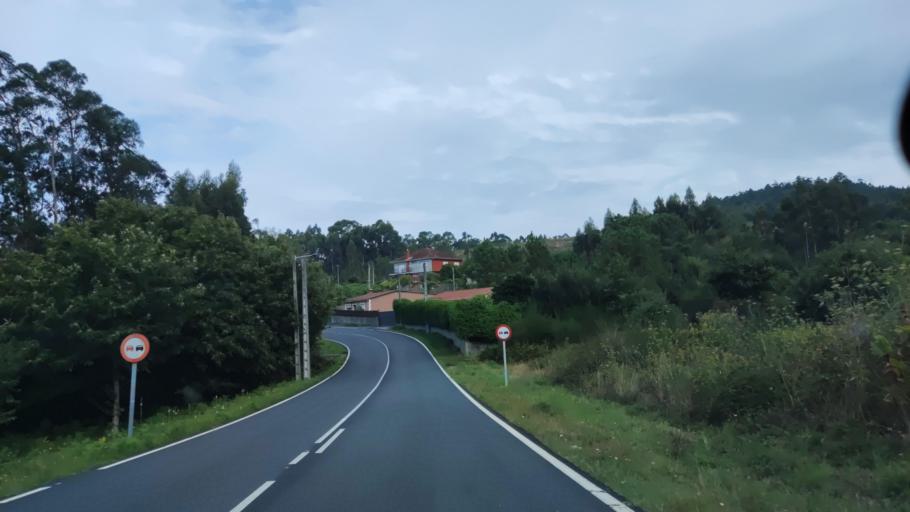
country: ES
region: Galicia
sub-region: Provincia de Pontevedra
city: Catoira
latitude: 42.6542
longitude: -8.7611
